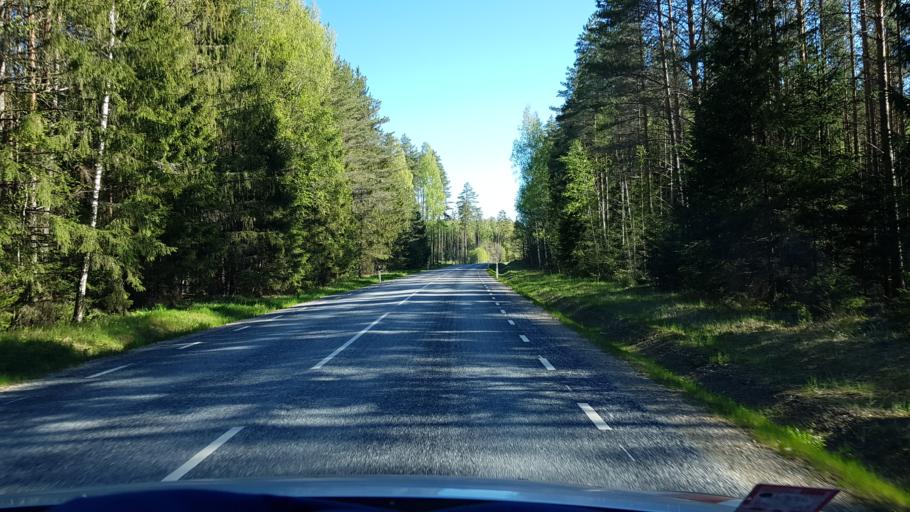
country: EE
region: Polvamaa
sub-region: Polva linn
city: Polva
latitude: 58.1388
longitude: 27.1598
